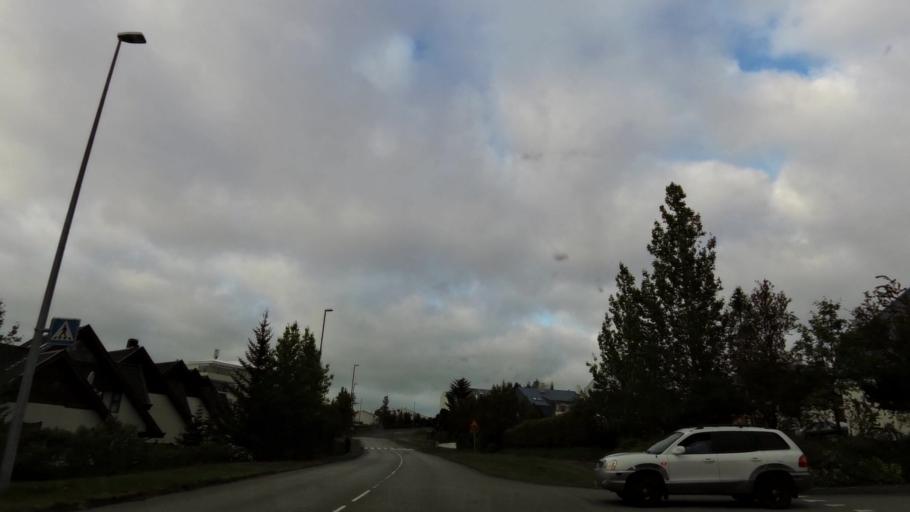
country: IS
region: Capital Region
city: Hafnarfjoerdur
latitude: 64.0593
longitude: -21.9549
